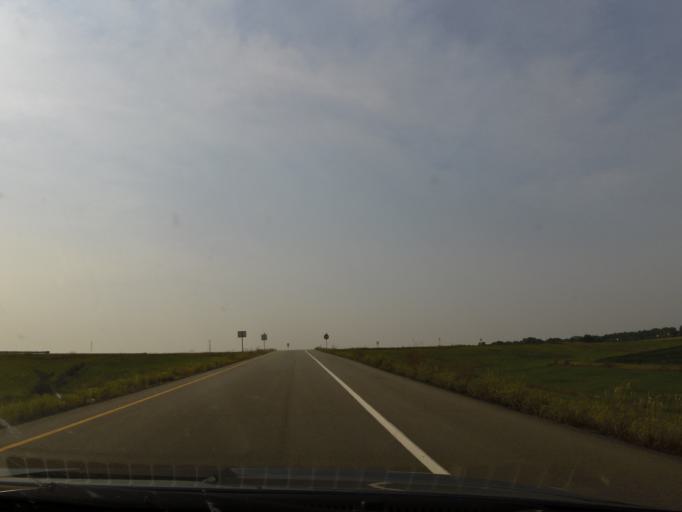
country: US
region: North Dakota
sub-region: Cass County
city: Horace
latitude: 46.6316
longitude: -96.8327
